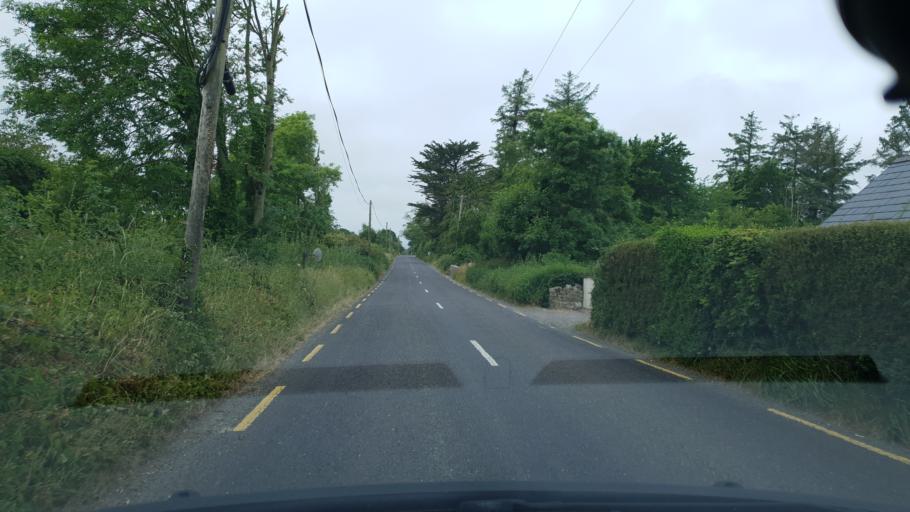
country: IE
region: Munster
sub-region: Ciarrai
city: Tralee
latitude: 52.1637
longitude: -9.6143
